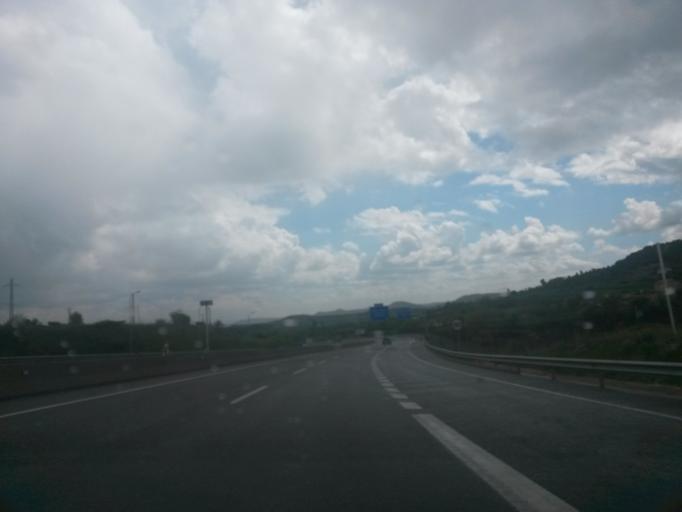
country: ES
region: Catalonia
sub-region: Provincia de Barcelona
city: Berga
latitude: 42.0940
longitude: 1.8542
